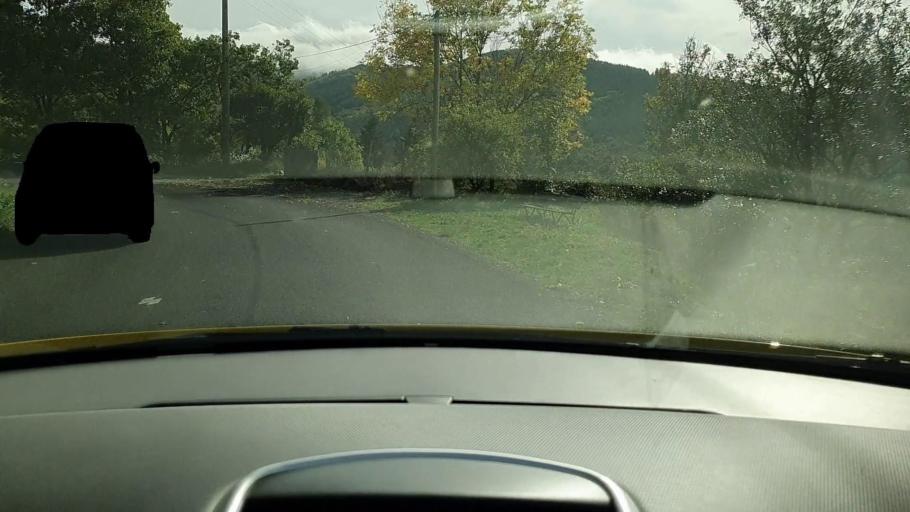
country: FR
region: Languedoc-Roussillon
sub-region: Departement de la Lozere
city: Meyrueis
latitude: 44.0672
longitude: 3.4405
